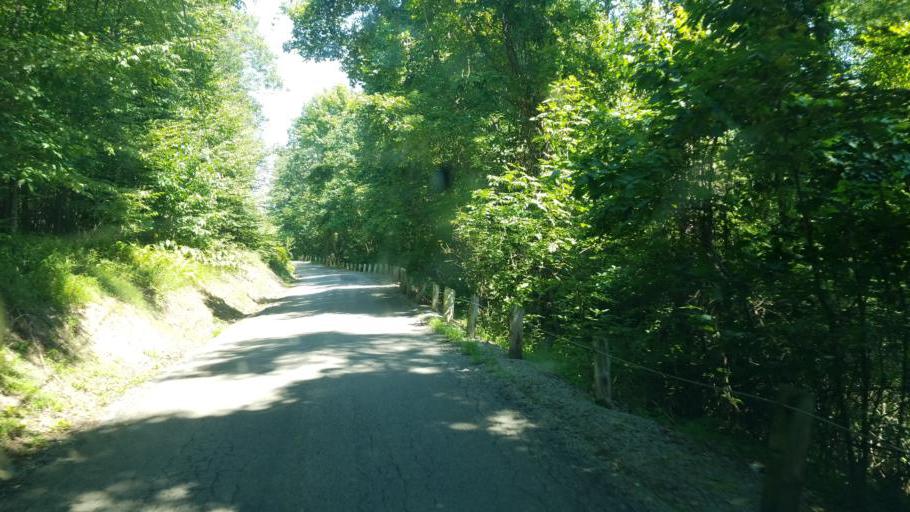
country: US
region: Pennsylvania
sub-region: Clarion County
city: Clarion
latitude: 41.1783
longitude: -79.4314
